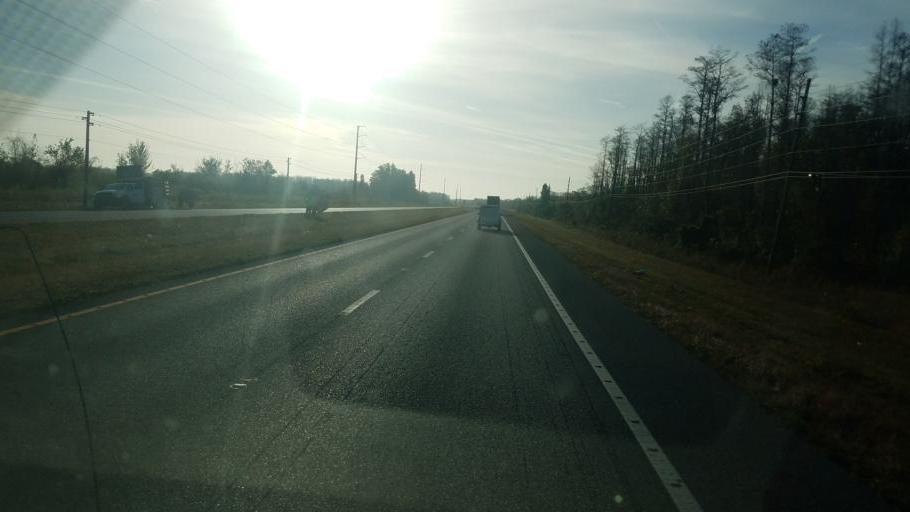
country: US
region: Florida
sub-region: Osceola County
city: Saint Cloud
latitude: 28.1583
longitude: -81.1133
